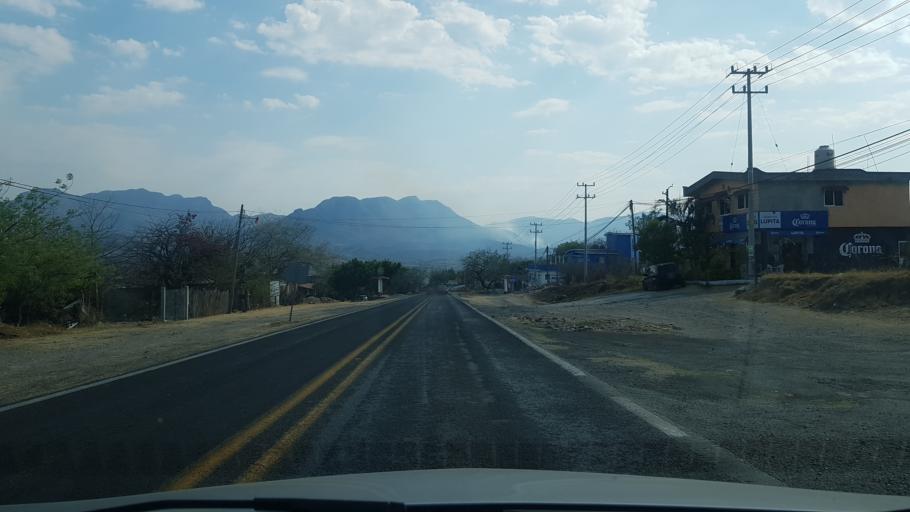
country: MX
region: Morelos
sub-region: Amacuzac
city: Amacuzac
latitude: 18.6067
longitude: -99.3633
